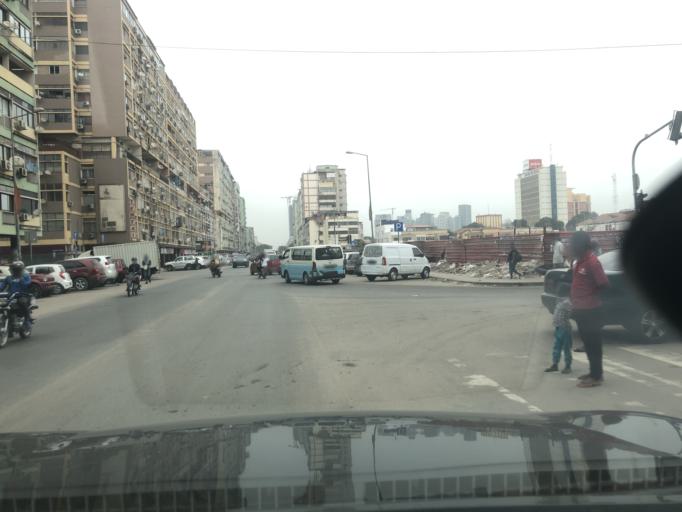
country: AO
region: Luanda
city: Luanda
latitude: -8.8191
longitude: 13.2513
